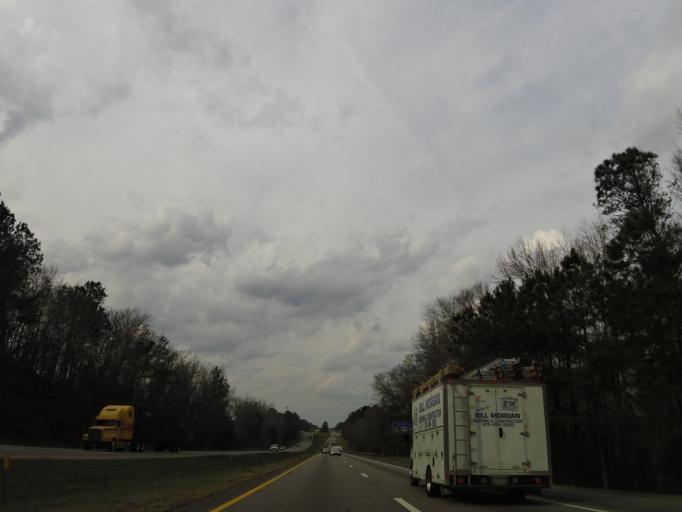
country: US
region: South Carolina
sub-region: Calhoun County
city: Saint Matthews
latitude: 33.6246
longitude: -80.8711
